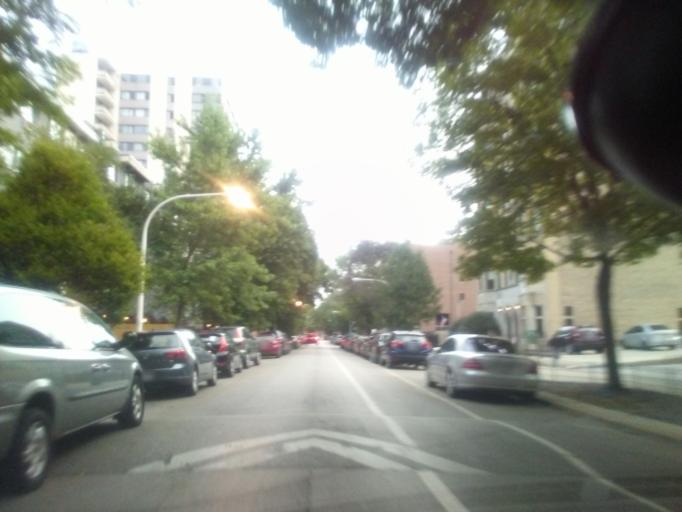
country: US
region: Illinois
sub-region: Cook County
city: Evanston
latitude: 41.9930
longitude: -87.6569
